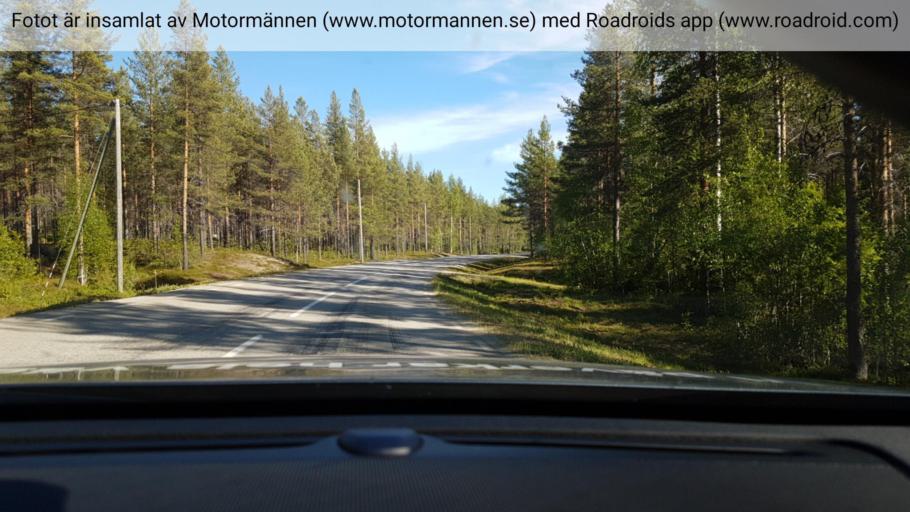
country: SE
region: Vaesterbotten
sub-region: Norsjo Kommun
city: Norsjoe
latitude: 64.7161
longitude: 19.1406
